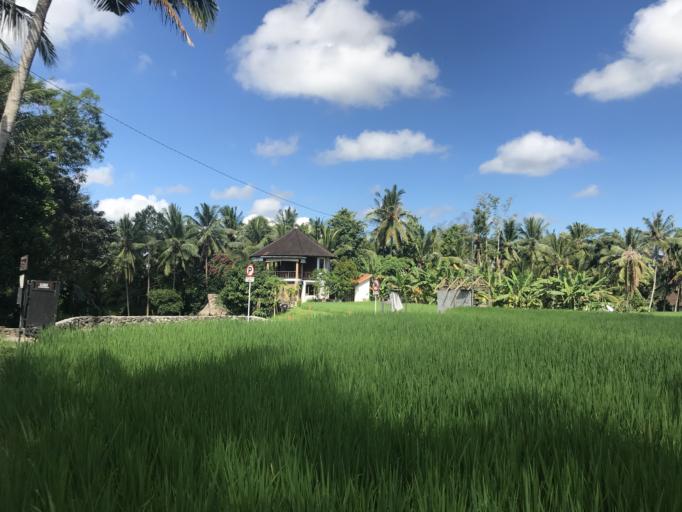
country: ID
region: Bali
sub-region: Kabupaten Gianyar
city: Ubud
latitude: -8.5015
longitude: 115.2579
